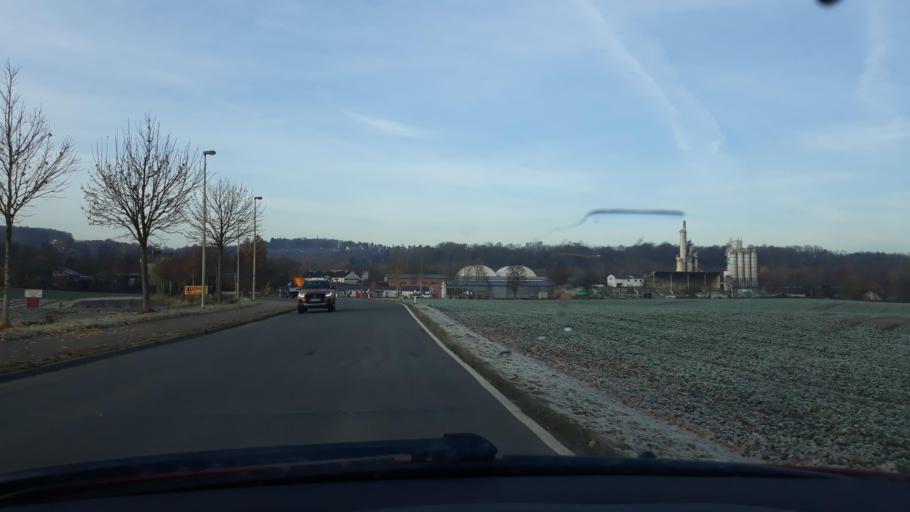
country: DE
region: Saxony
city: Wilkau-Hasslau
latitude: 50.6877
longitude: 12.5046
